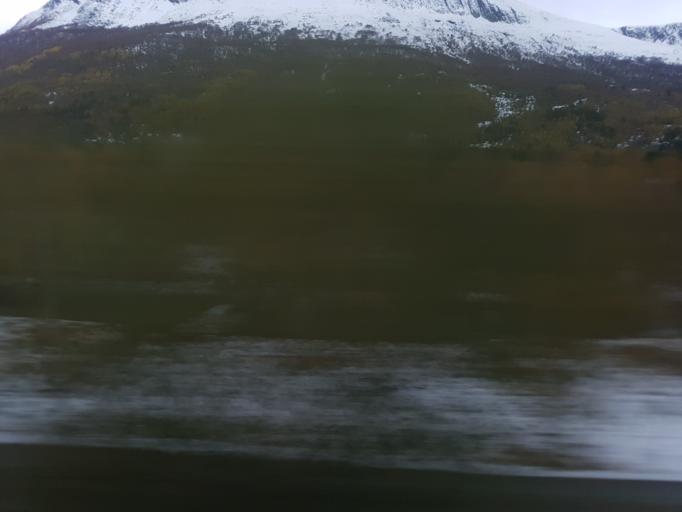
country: NO
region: Sor-Trondelag
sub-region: Oppdal
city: Oppdal
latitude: 62.5095
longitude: 9.5992
